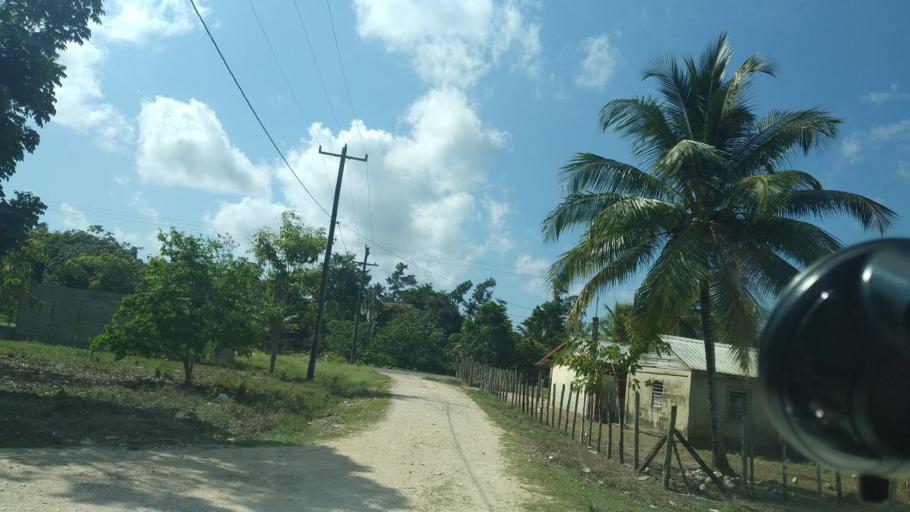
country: BZ
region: Stann Creek
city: Placencia
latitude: 16.4714
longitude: -88.6253
